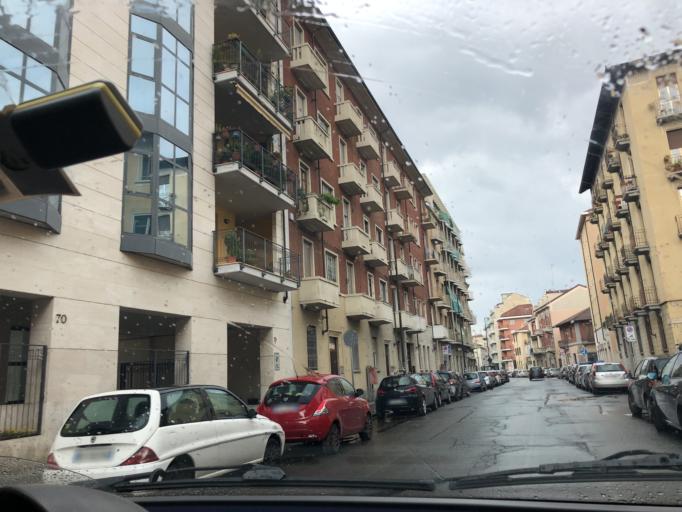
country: IT
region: Piedmont
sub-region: Provincia di Torino
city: Lesna
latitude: 45.0793
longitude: 7.6309
